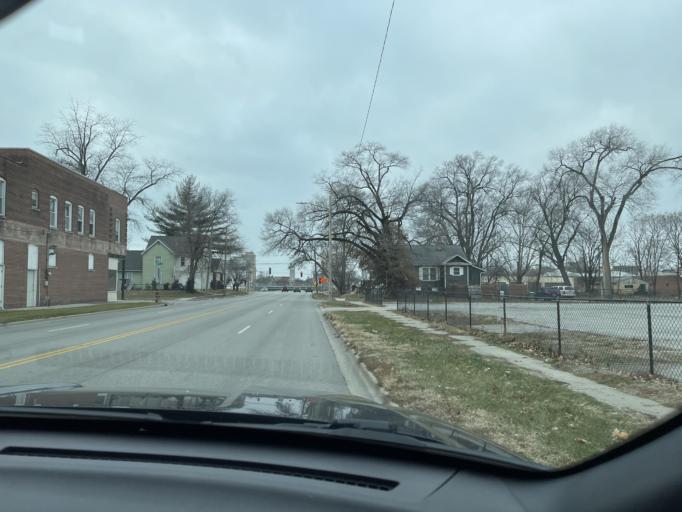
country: US
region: Illinois
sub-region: Sangamon County
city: Springfield
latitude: 39.7948
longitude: -89.6389
